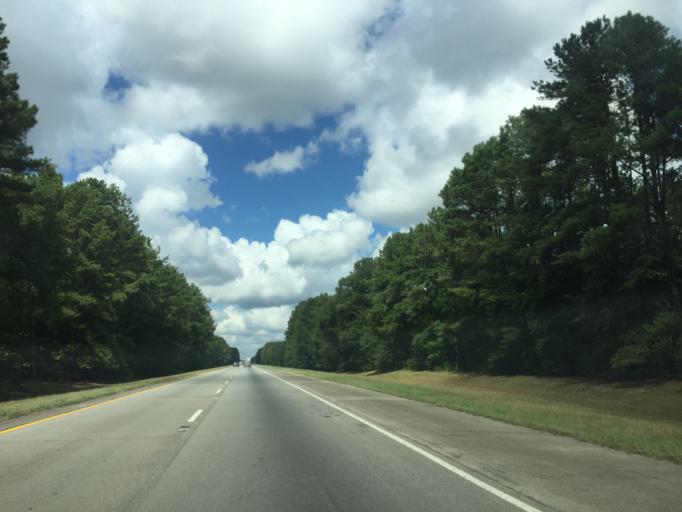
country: US
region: Georgia
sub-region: Candler County
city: Metter
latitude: 32.3858
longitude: -82.2512
